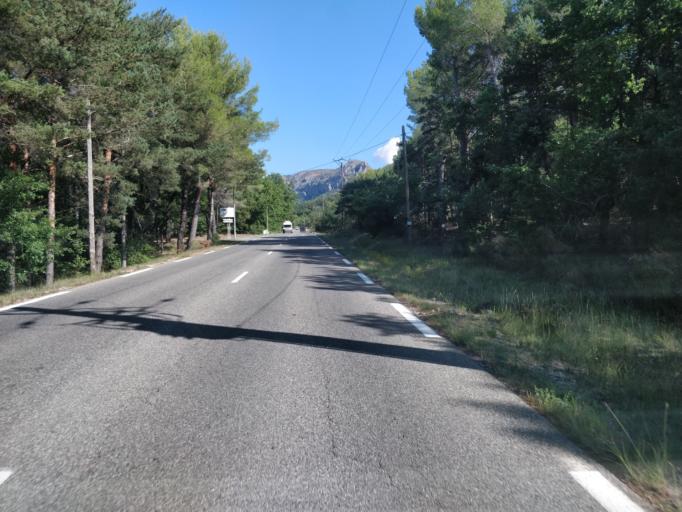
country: FR
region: Provence-Alpes-Cote d'Azur
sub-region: Departement des Alpes-de-Haute-Provence
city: Riez
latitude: 43.8141
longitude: 6.2264
